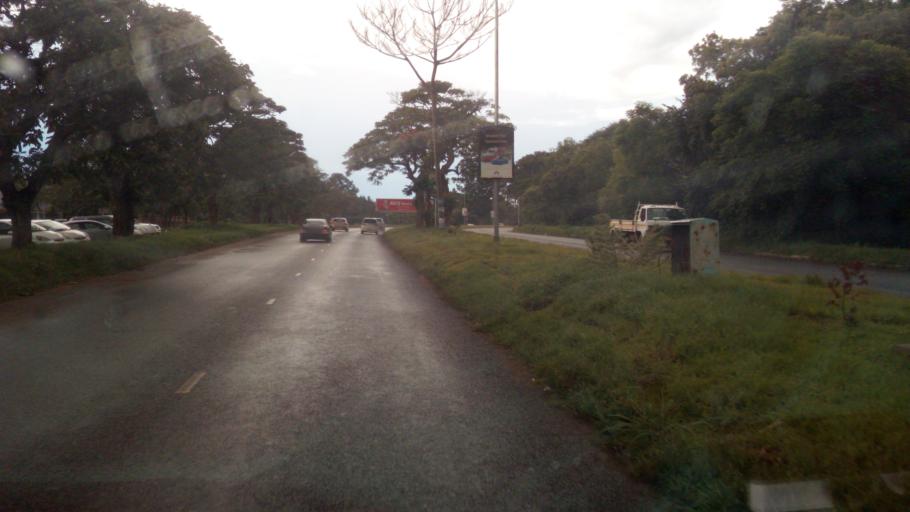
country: ZW
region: Harare
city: Harare
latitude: -17.7960
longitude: 31.0626
